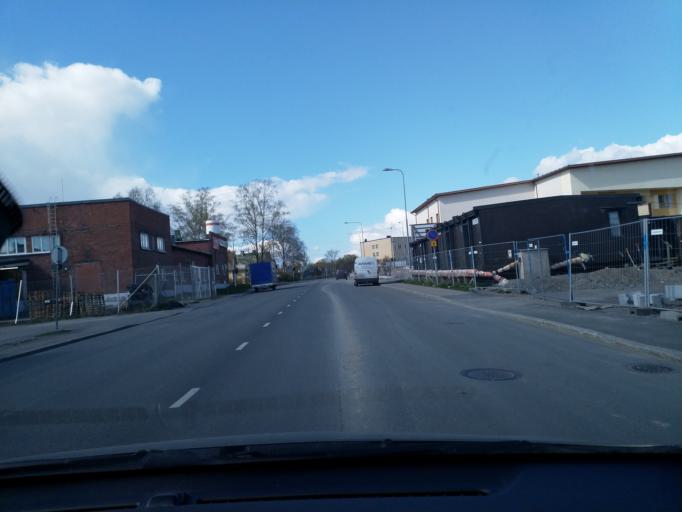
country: FI
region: Pirkanmaa
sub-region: Tampere
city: Tampere
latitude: 61.4813
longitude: 23.7895
